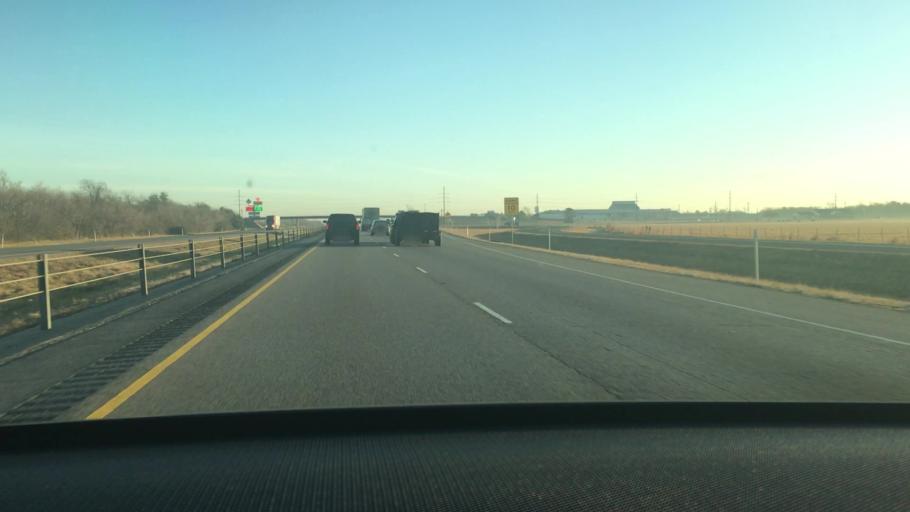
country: US
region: Texas
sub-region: Jefferson County
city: Fannett
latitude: 29.9829
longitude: -94.2128
